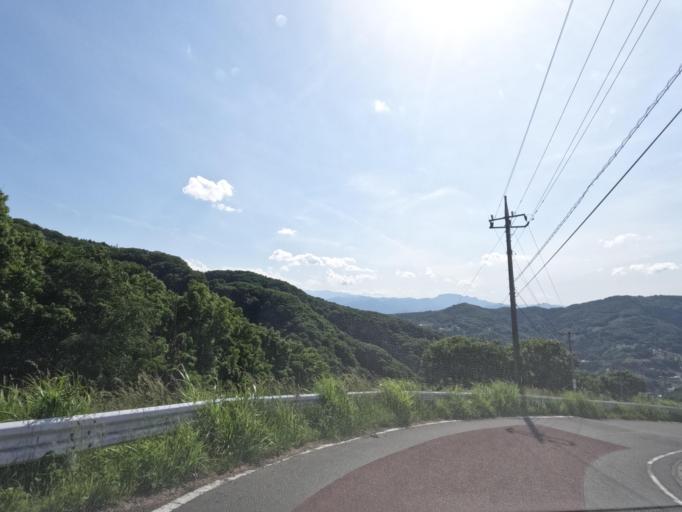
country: JP
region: Saitama
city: Yorii
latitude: 36.0494
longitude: 139.1505
